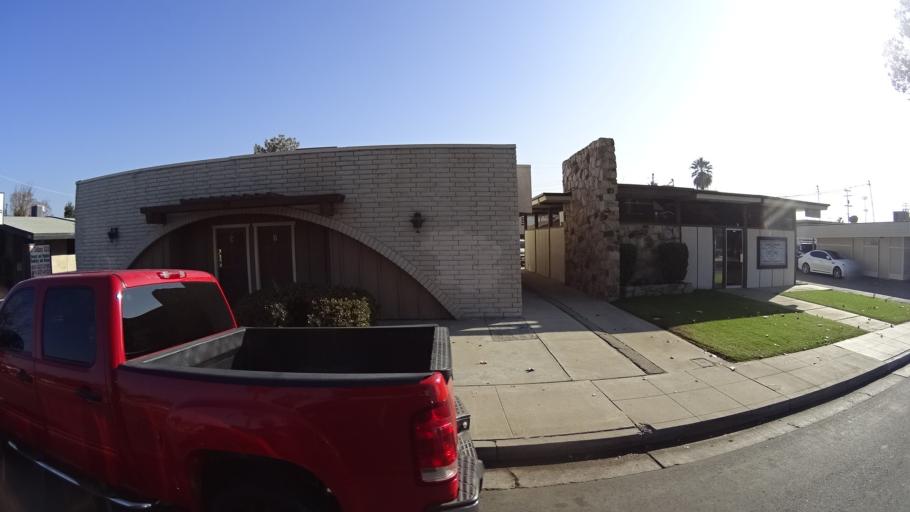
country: US
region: California
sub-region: Kern County
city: Bakersfield
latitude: 35.3556
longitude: -119.0213
